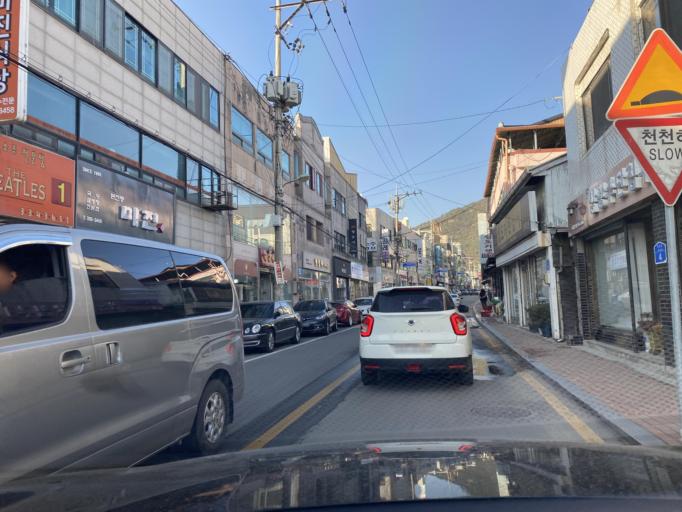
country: KR
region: Chungcheongnam-do
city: Yesan
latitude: 36.6784
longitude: 126.8497
